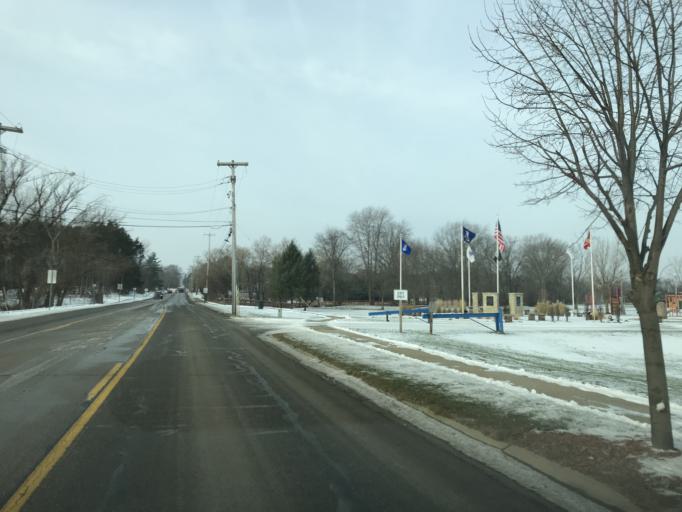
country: US
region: Michigan
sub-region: Kent County
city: Byron Center
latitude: 42.7252
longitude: -85.7285
